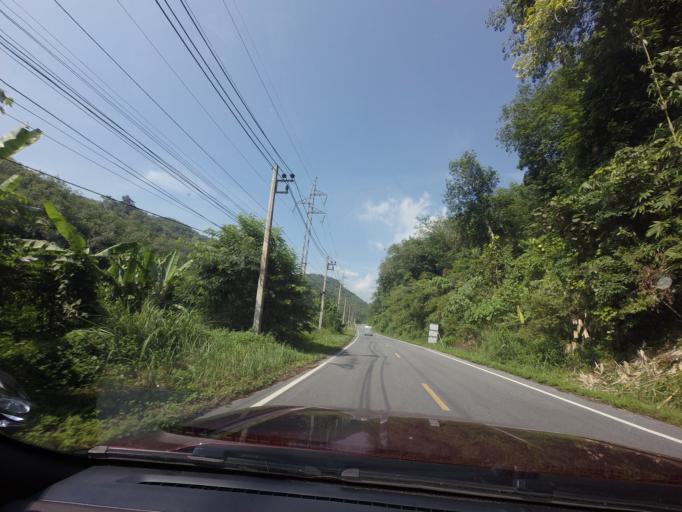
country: TH
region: Yala
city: Betong
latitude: 5.9465
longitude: 101.1902
